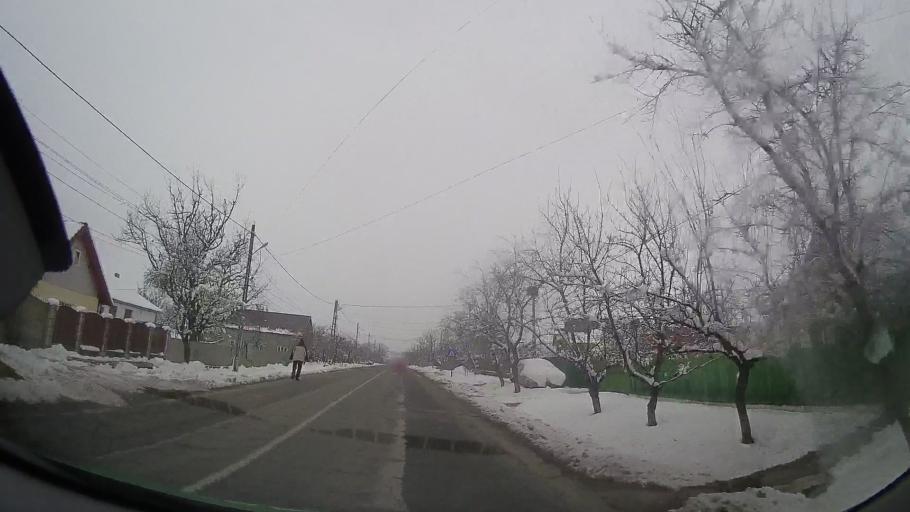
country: RO
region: Vaslui
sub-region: Comuna Negresti
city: Negresti
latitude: 46.8390
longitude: 27.4108
